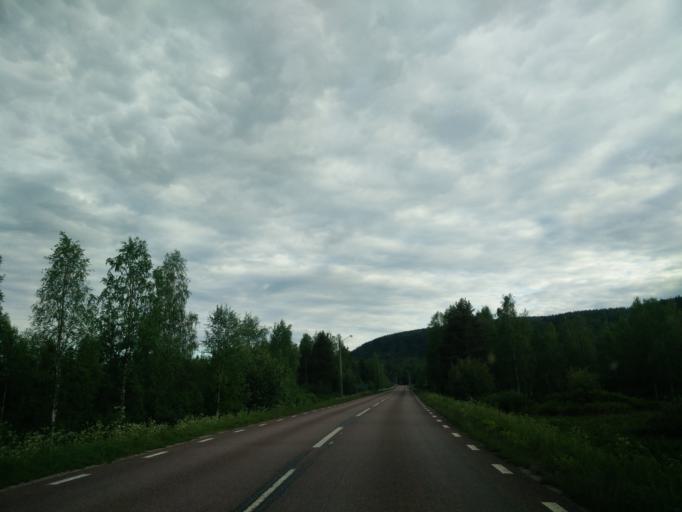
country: SE
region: Jaemtland
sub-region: Harjedalens Kommun
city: Sveg
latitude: 62.2772
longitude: 14.8065
